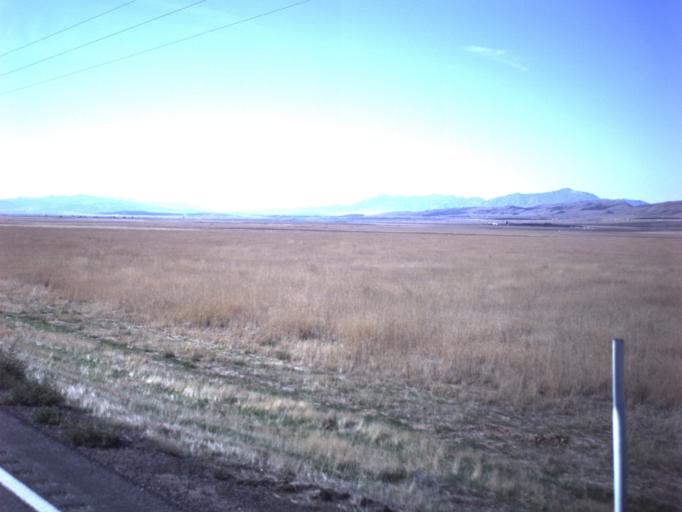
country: US
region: Utah
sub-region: Juab County
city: Nephi
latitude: 39.6120
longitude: -111.8618
